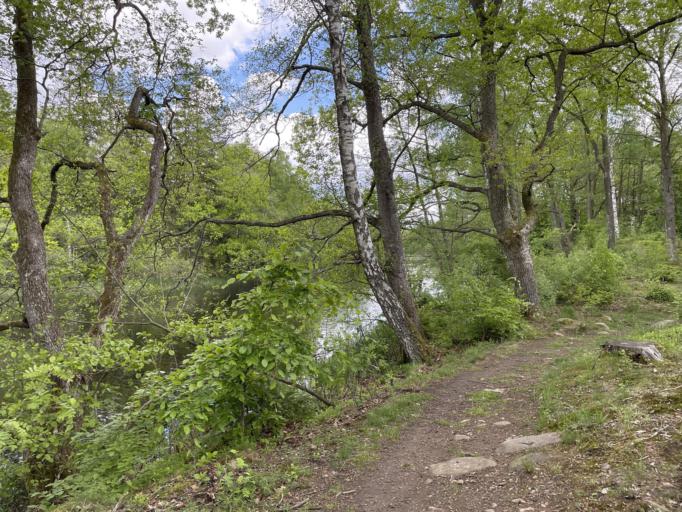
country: SE
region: Skane
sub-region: Klippans Kommun
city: Klippan
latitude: 56.1599
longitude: 13.1578
